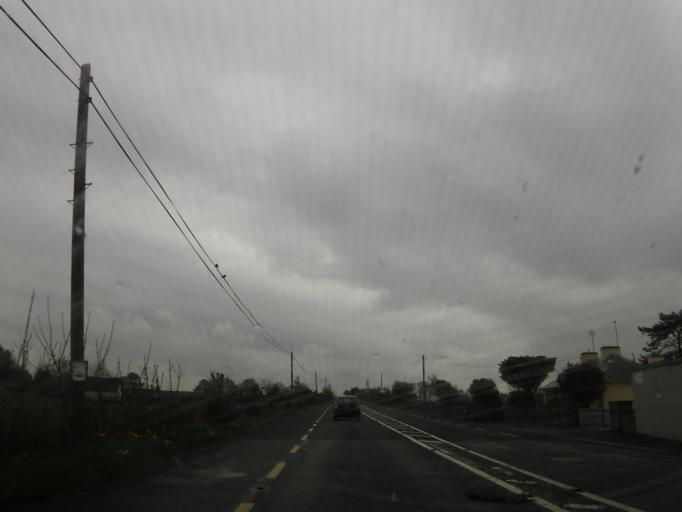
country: IE
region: Connaught
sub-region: County Galway
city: Tuam
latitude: 53.4380
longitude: -8.9052
